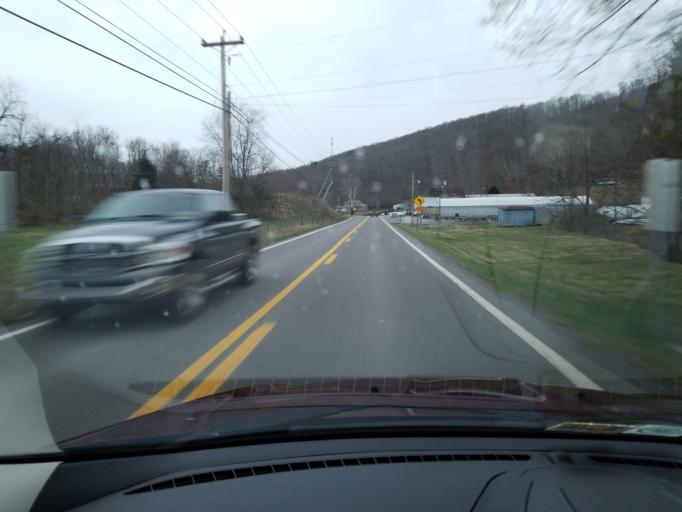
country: US
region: Virginia
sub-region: Giles County
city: Pearisburg
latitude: 37.4011
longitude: -80.7683
